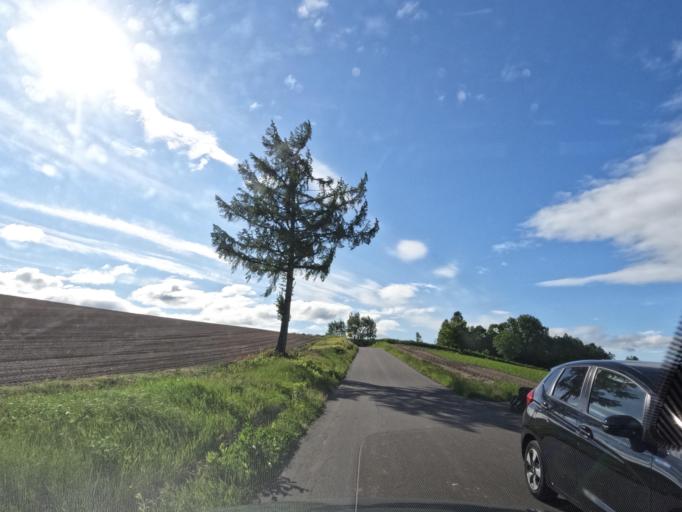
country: JP
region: Hokkaido
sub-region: Asahikawa-shi
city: Asahikawa
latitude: 43.5982
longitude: 142.4283
